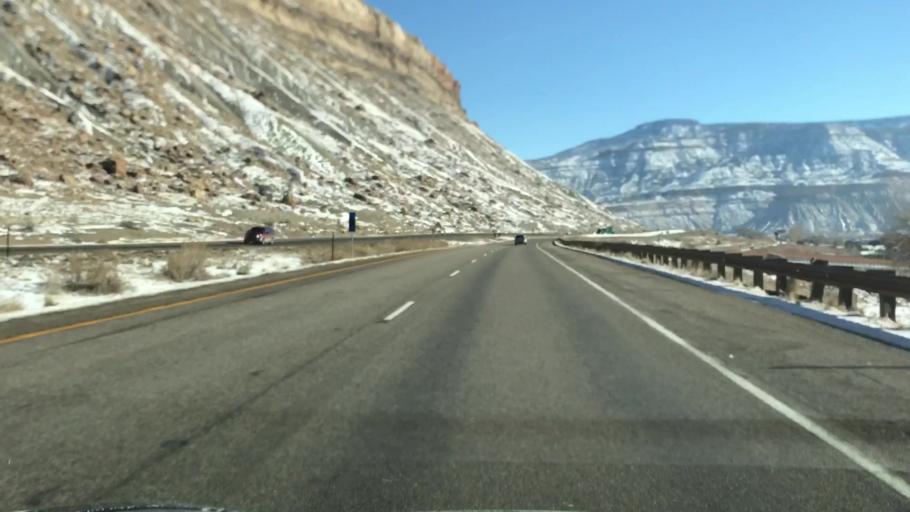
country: US
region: Colorado
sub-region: Mesa County
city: Palisade
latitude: 39.1203
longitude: -108.3696
